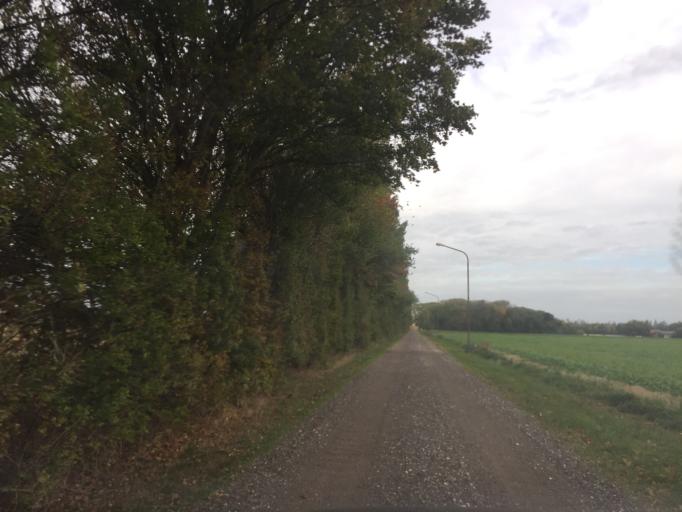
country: DK
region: Zealand
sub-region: Lolland Kommune
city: Rodbyhavn
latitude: 54.6660
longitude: 11.3462
